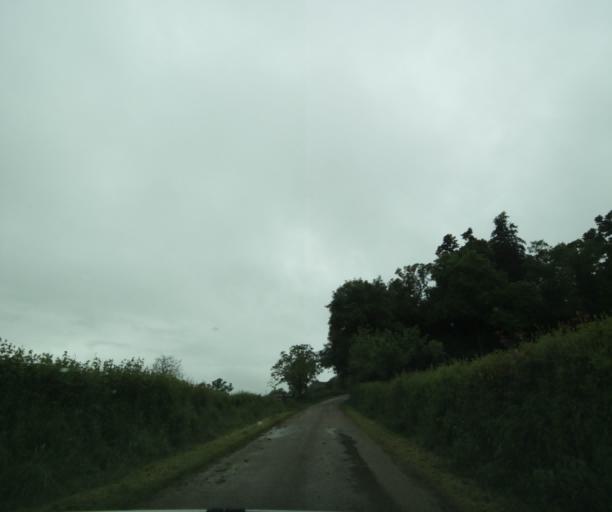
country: FR
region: Bourgogne
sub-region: Departement de Saone-et-Loire
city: Charolles
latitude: 46.3795
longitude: 4.2402
